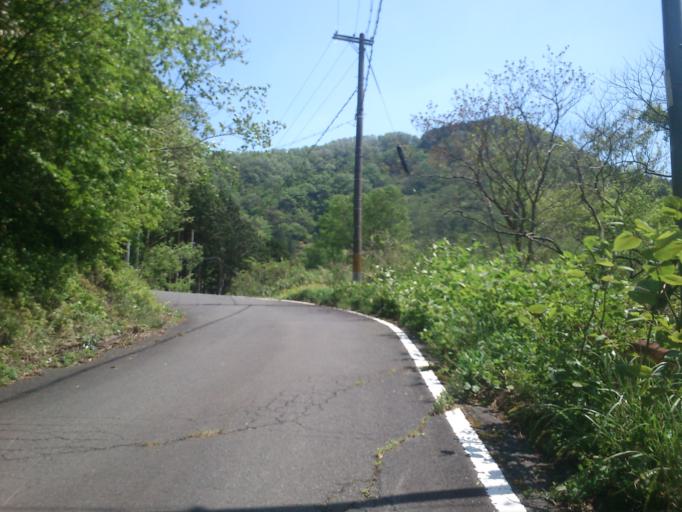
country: JP
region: Kyoto
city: Miyazu
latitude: 35.6983
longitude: 135.1579
